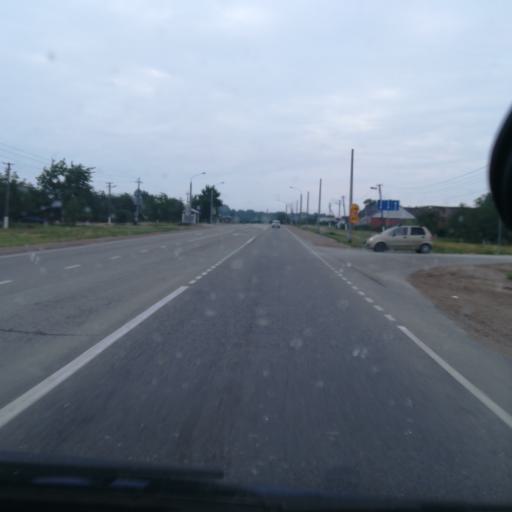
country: RU
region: Krasnodarskiy
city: Kiyevskoye
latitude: 44.9962
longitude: 37.9410
